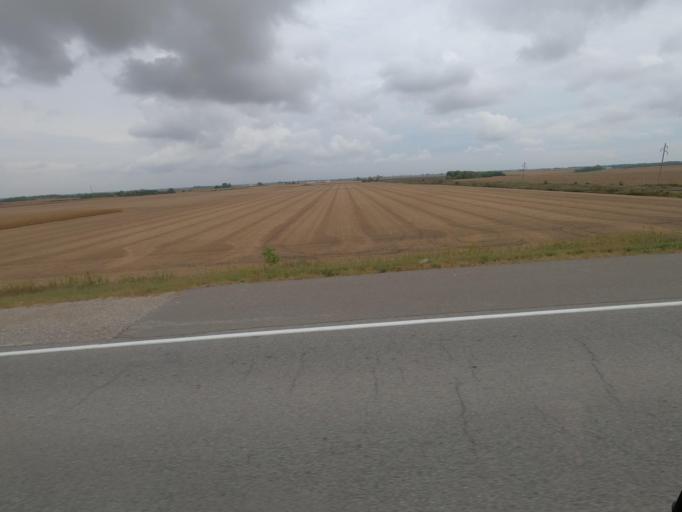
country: US
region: Iowa
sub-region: Wapello County
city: Ottumwa
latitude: 40.9915
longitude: -92.2368
